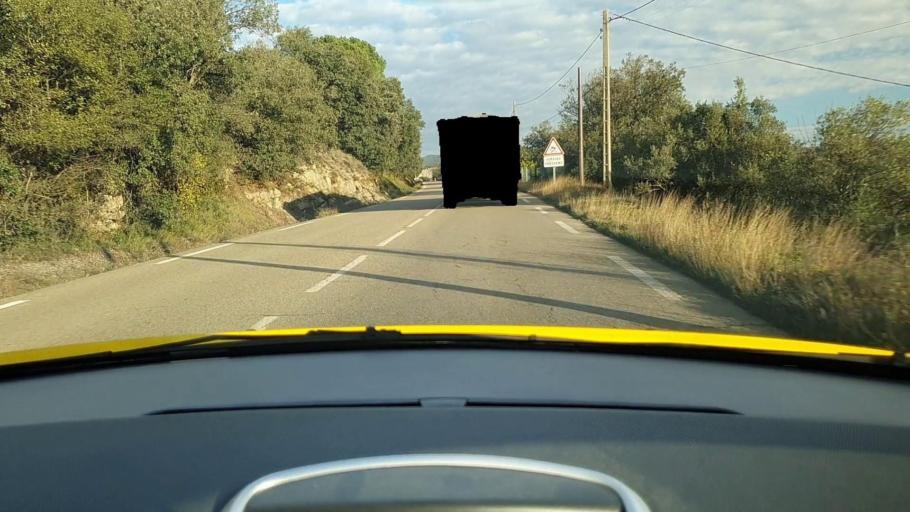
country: FR
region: Languedoc-Roussillon
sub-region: Departement du Gard
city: Saint-Martin-de-Valgalgues
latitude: 44.1694
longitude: 4.0835
